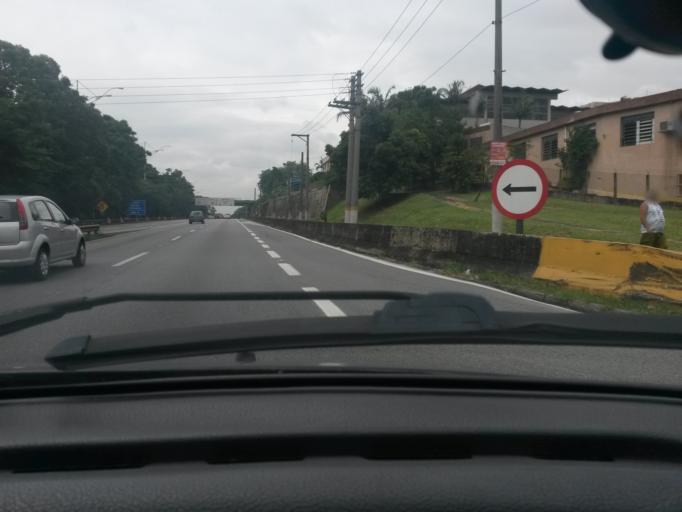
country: BR
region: Sao Paulo
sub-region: Sao Caetano Do Sul
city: Sao Caetano do Sul
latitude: -23.6246
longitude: -46.6000
